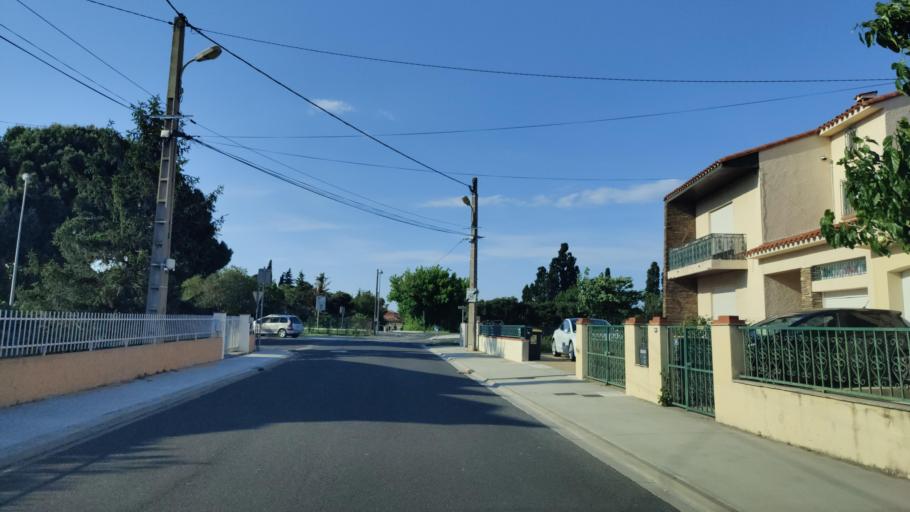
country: FR
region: Languedoc-Roussillon
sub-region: Departement des Pyrenees-Orientales
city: Elne
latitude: 42.6042
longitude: 2.9688
